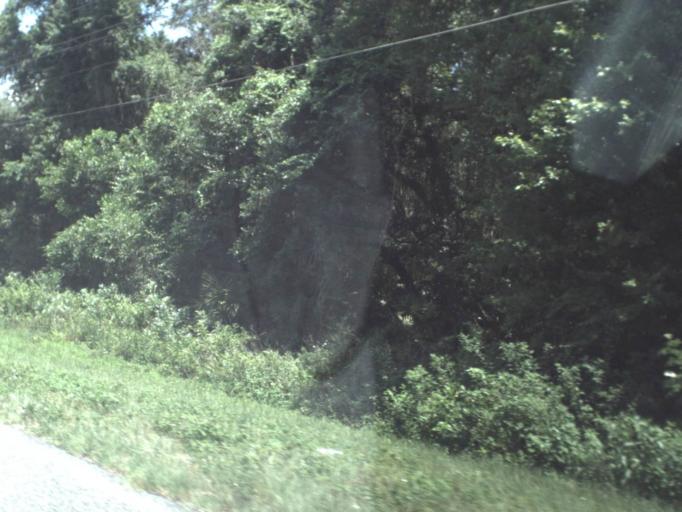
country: US
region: Florida
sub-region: Putnam County
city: Crescent City
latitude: 29.4708
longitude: -81.5311
